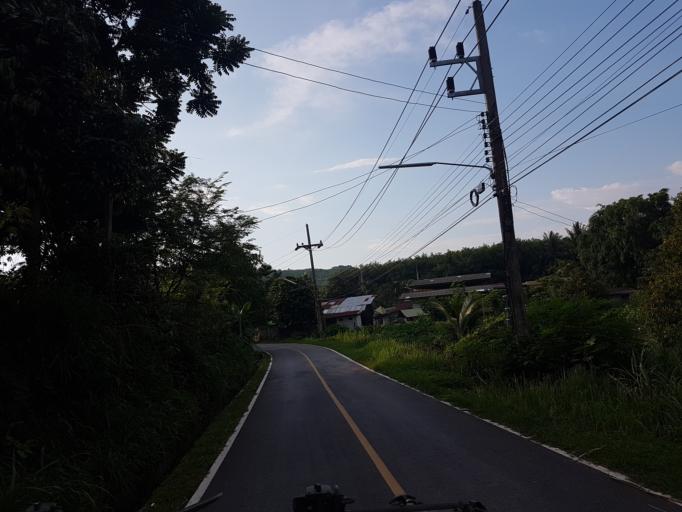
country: TH
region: Pattani
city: Khok Pho
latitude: 6.6754
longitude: 101.0946
